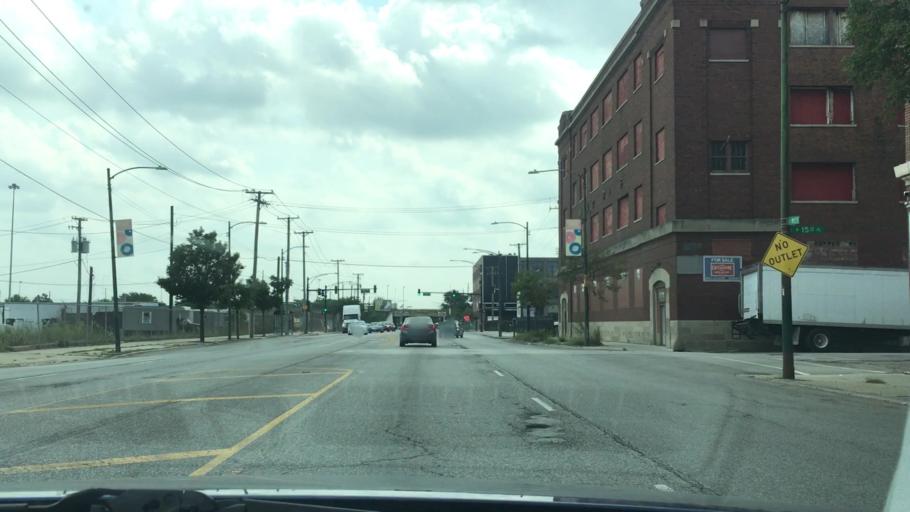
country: US
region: Illinois
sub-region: Cook County
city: Chicago
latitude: 41.8605
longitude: -87.6859
